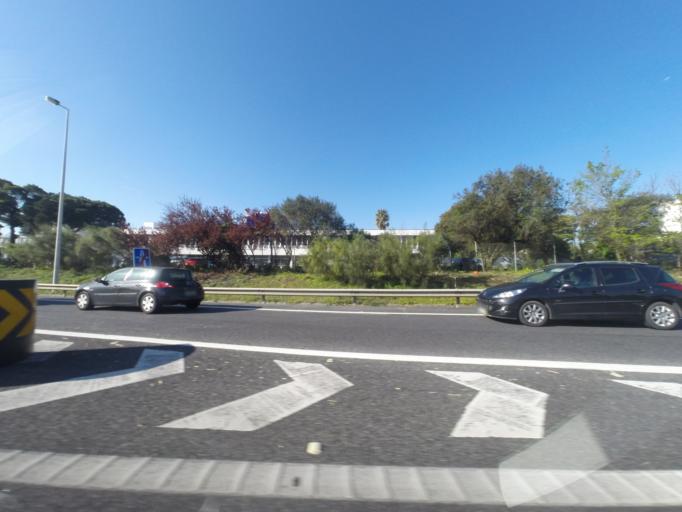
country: PT
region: Lisbon
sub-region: Oeiras
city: Linda-a-Velha
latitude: 38.7189
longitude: -9.2375
